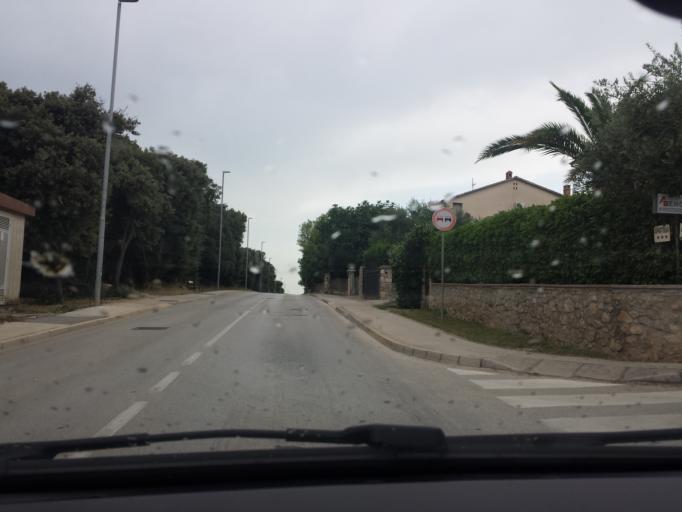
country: HR
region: Istarska
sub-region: Grad Pula
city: Pula
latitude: 44.9005
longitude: 13.8523
